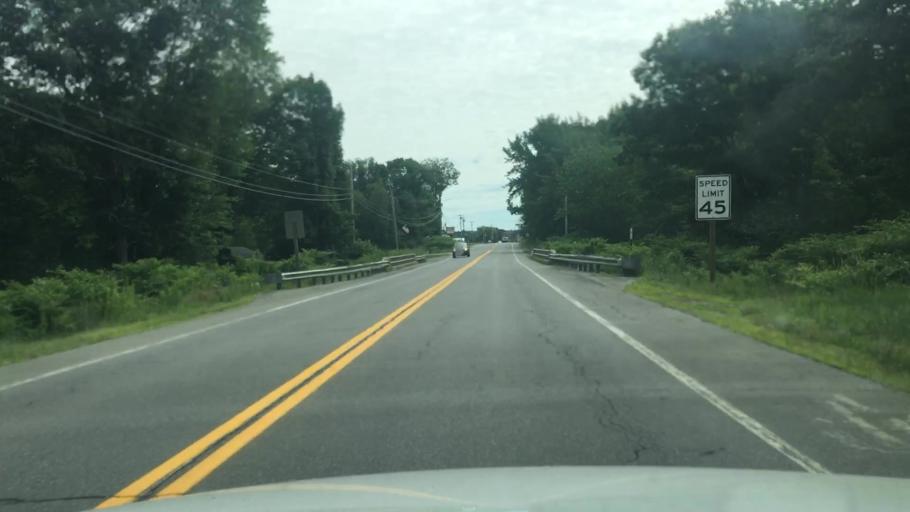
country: US
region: Maine
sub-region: Waldo County
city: Burnham
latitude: 44.6133
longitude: -69.3556
